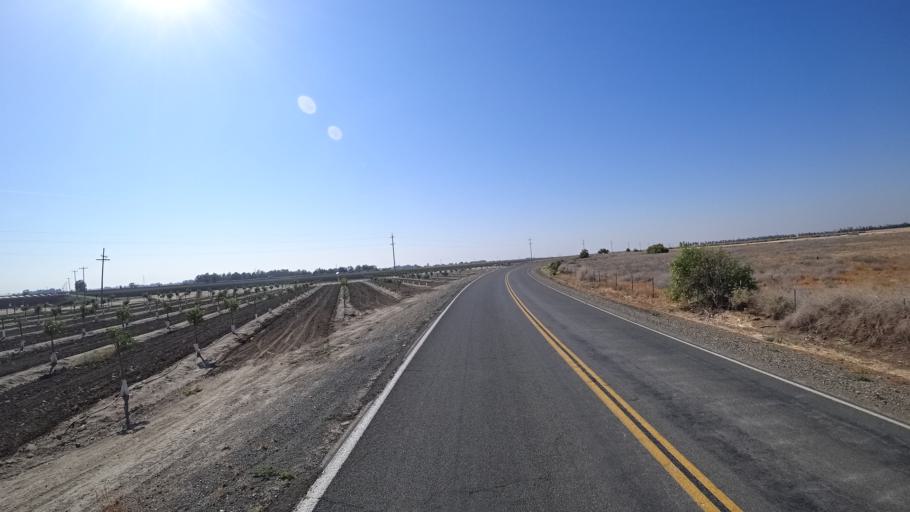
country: US
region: California
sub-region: Fresno County
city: Riverdale
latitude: 36.3574
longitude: -119.9059
